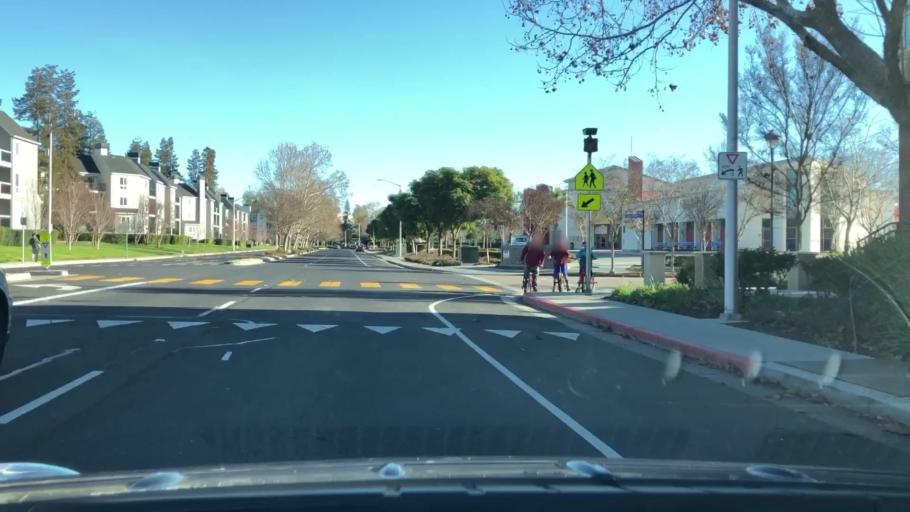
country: US
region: California
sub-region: Santa Clara County
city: Santa Clara
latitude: 37.3996
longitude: -121.9476
